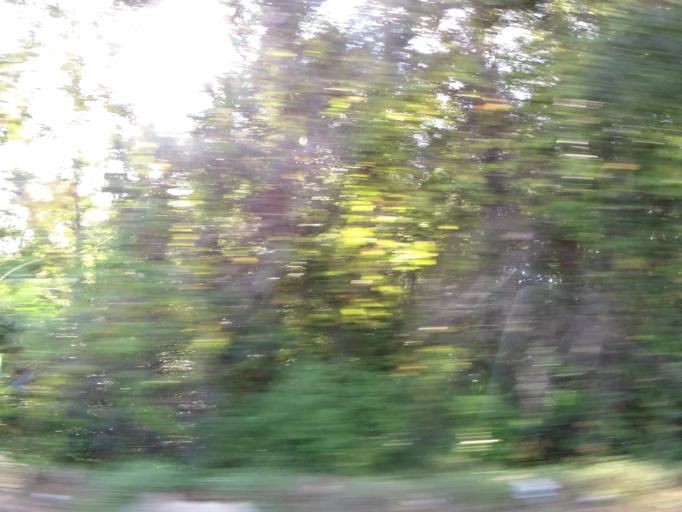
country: US
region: Georgia
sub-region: Brooks County
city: Quitman
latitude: 30.7777
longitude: -83.5605
